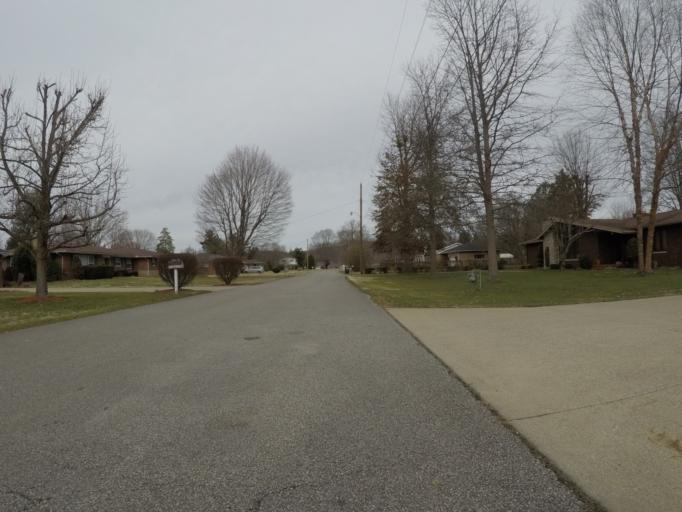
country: US
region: West Virginia
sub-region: Cabell County
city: Pea Ridge
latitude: 38.4468
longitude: -82.3407
